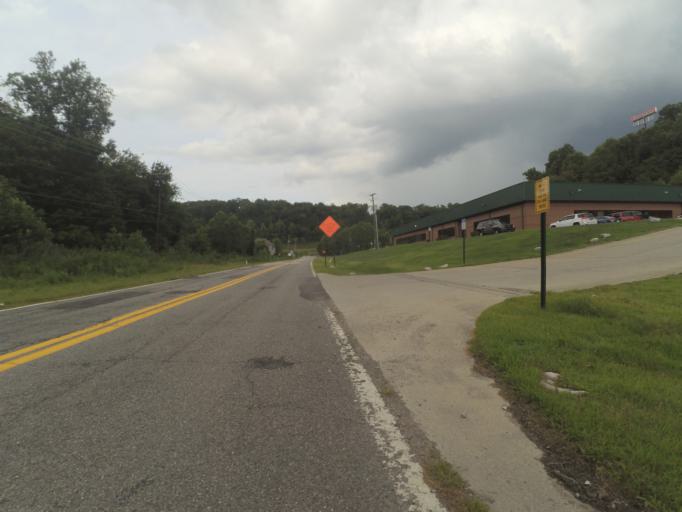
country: US
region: West Virginia
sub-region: Cabell County
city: Huntington
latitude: 38.3889
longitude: -82.4005
